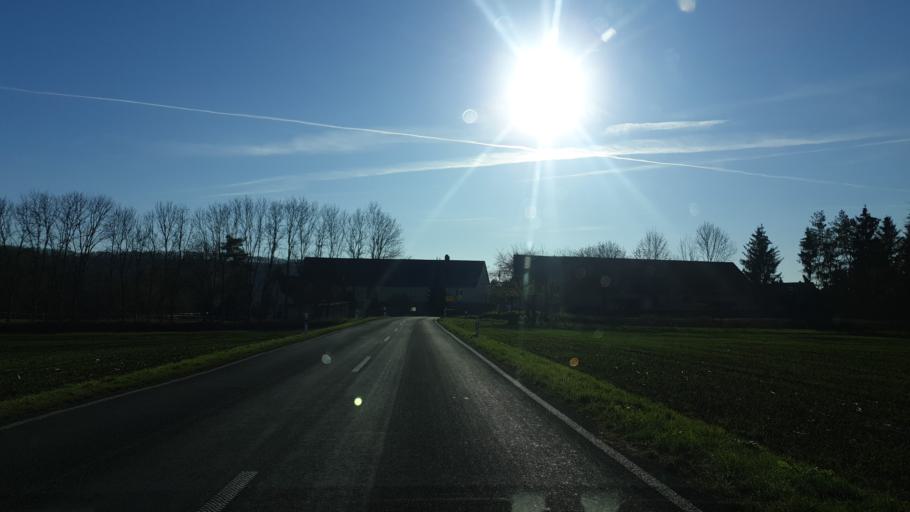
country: DE
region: Thuringia
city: Hartmannsdorf
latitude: 50.9867
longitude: 11.9885
